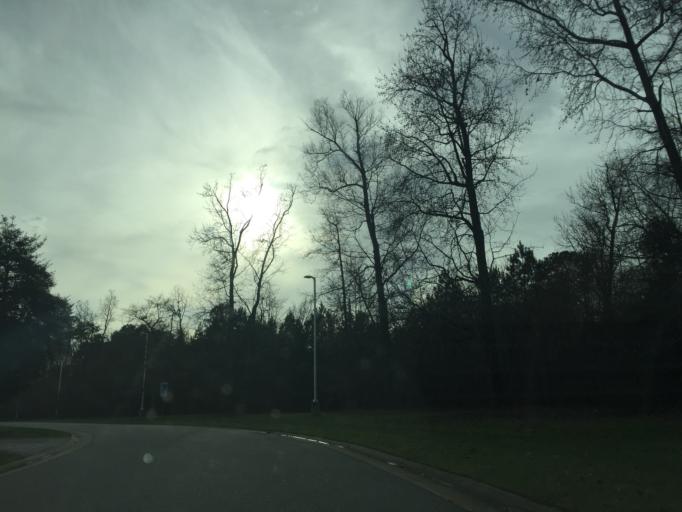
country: US
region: Virginia
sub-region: City of Newport News
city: Newport News
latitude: 37.0555
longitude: -76.4898
